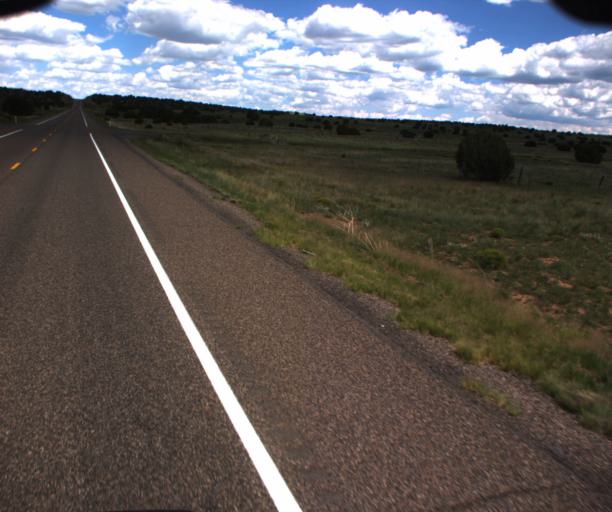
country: US
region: Arizona
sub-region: Apache County
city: Springerville
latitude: 34.1532
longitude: -109.1488
